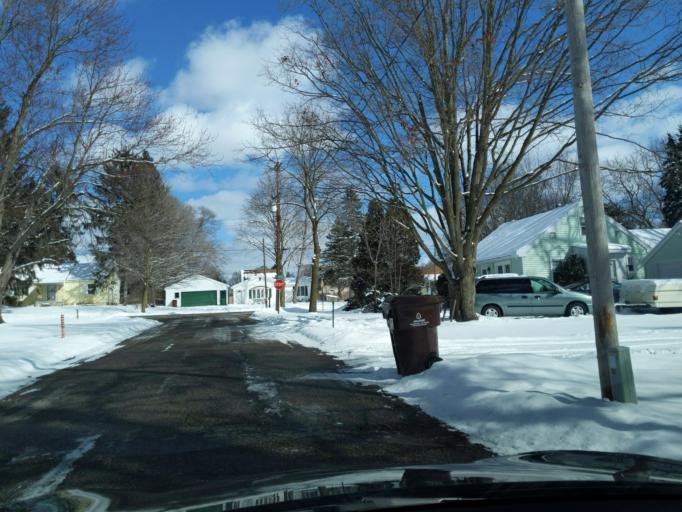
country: US
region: Michigan
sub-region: Eaton County
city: Dimondale
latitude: 42.6458
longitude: -84.6467
